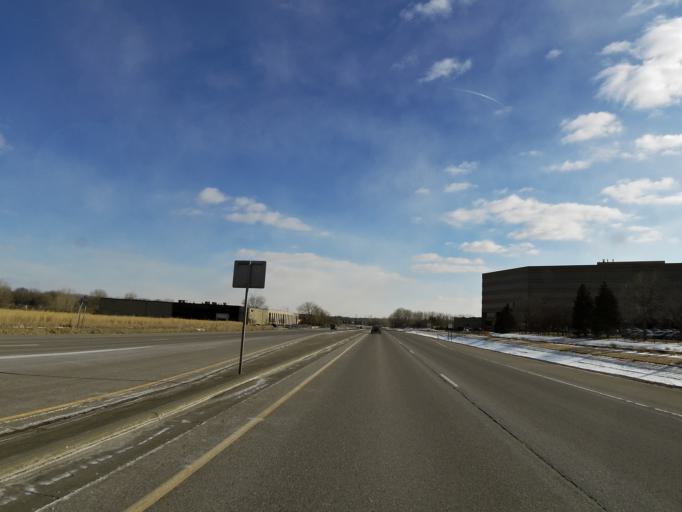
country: US
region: Minnesota
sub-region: Dakota County
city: Eagan
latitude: 44.8267
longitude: -93.1117
